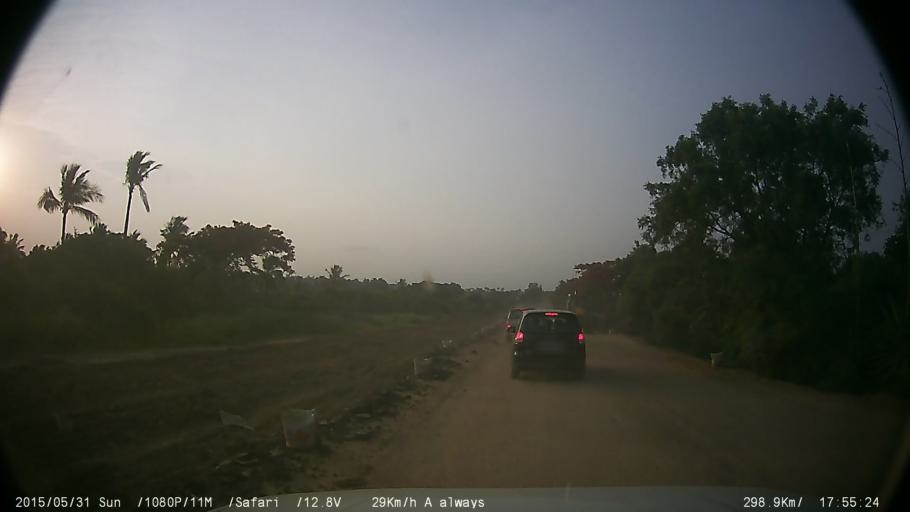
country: IN
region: Karnataka
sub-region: Mysore
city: Nanjangud
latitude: 11.9908
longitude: 76.6700
